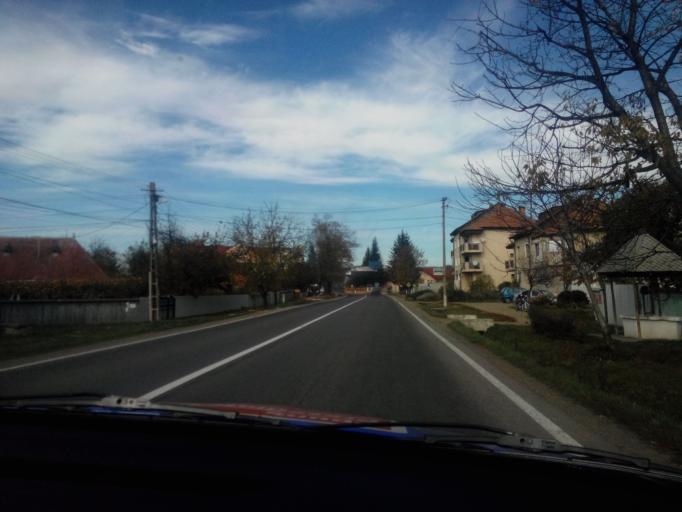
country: RO
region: Bacau
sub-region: Comuna Sanduleni
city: Sanduleni
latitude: 46.4388
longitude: 26.7377
